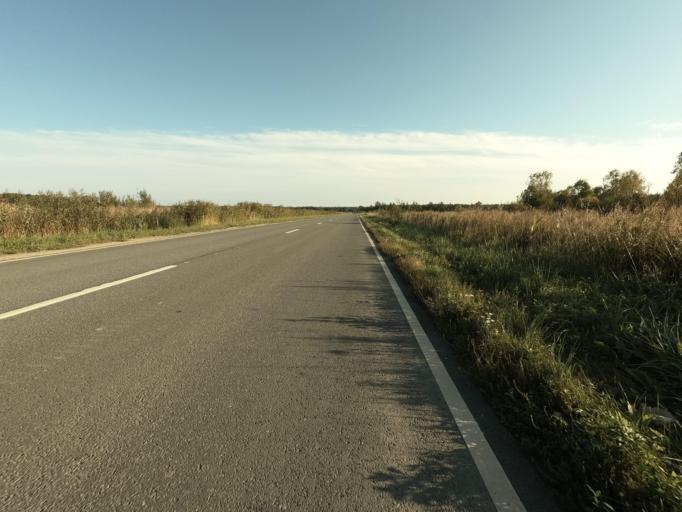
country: RU
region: St.-Petersburg
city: Sapernyy
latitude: 59.7339
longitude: 30.6570
